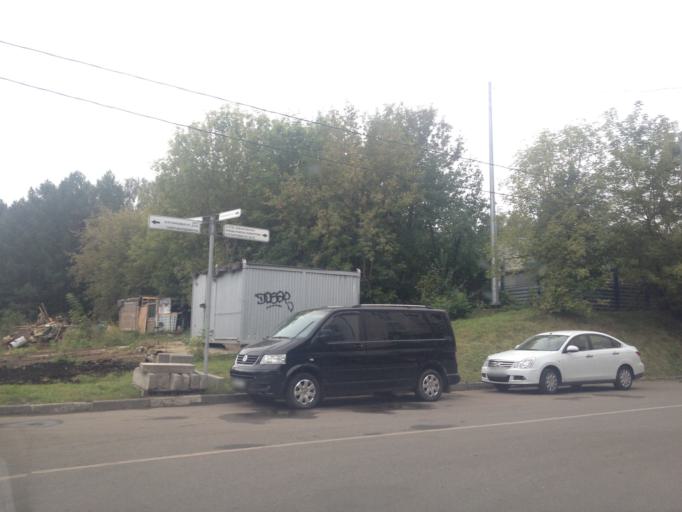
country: RU
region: Moskovskaya
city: Izmaylovo
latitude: 55.7887
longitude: 37.7942
